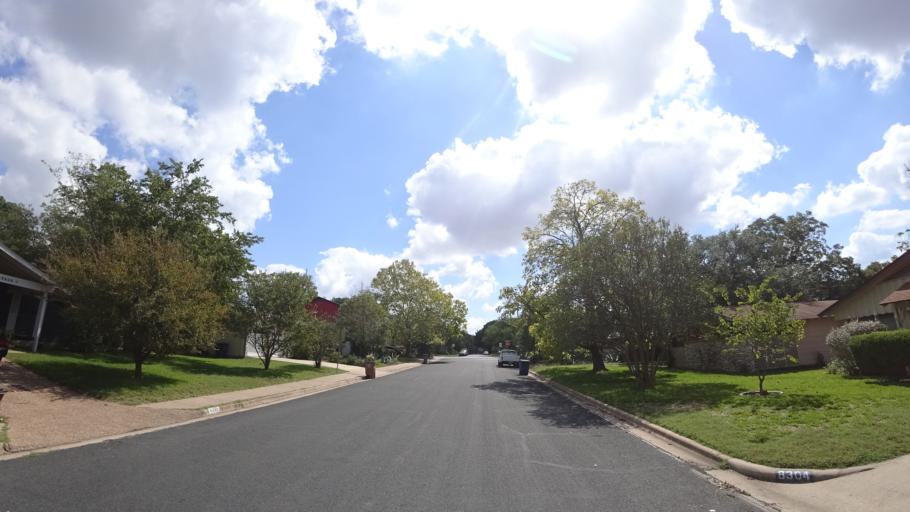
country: US
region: Texas
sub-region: Travis County
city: Wells Branch
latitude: 30.3618
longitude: -97.7236
